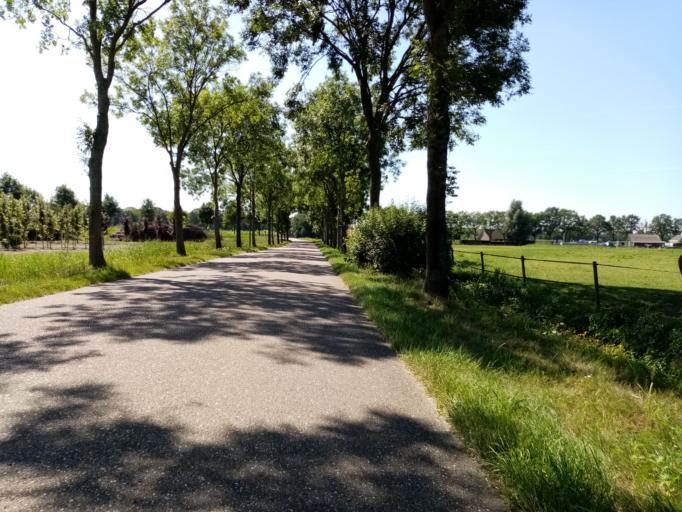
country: NL
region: North Brabant
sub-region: Gemeente Breda
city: Breda
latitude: 51.6273
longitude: 4.7018
